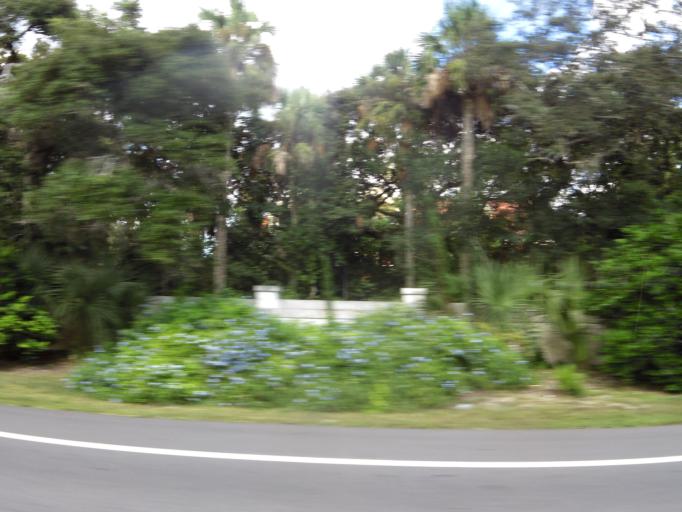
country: US
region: Florida
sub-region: Saint Johns County
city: Palm Valley
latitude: 30.1302
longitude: -81.3491
